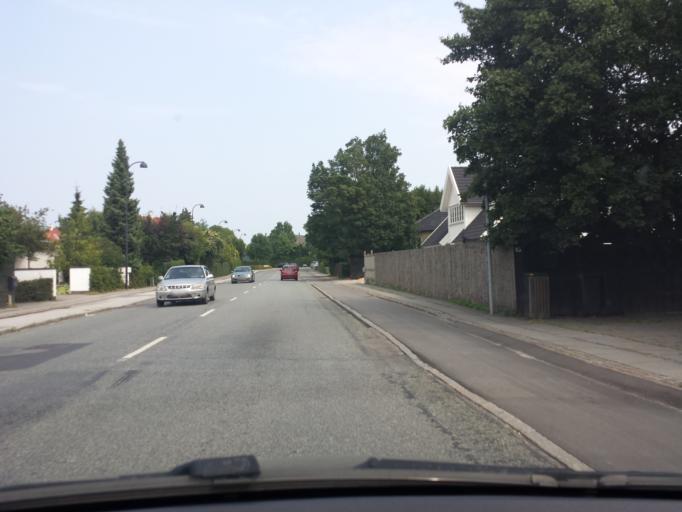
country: DK
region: Capital Region
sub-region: Gentofte Kommune
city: Charlottenlund
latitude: 55.7731
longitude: 12.5821
